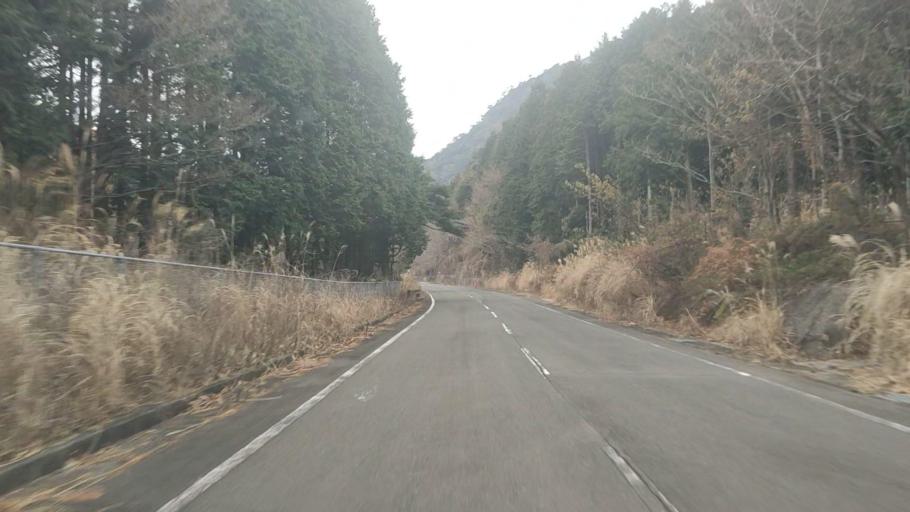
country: JP
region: Nagasaki
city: Shimabara
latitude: 32.7837
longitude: 130.2789
